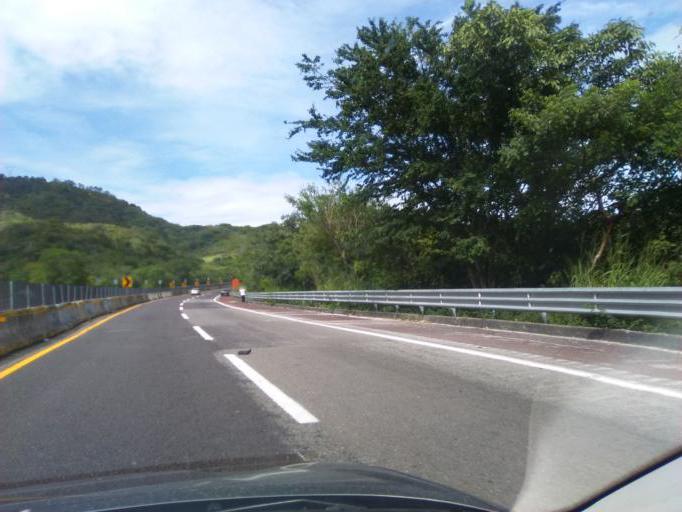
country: MX
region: Guerrero
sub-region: Chilpancingo de los Bravo
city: Acahuizotla
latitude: 17.3686
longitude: -99.4804
